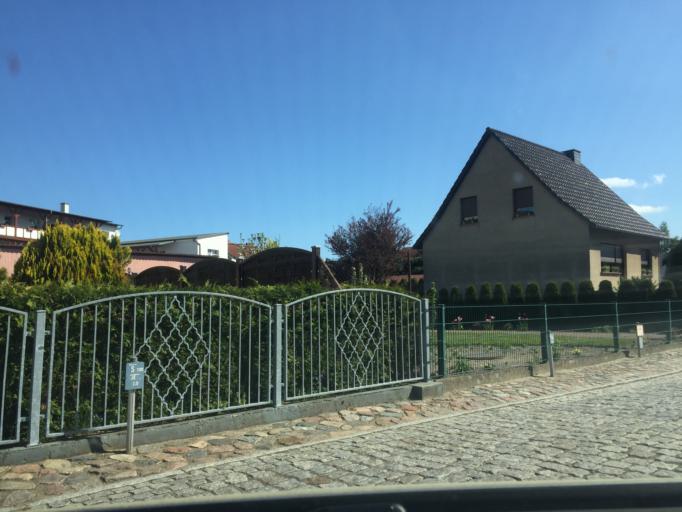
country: DE
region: Mecklenburg-Vorpommern
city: Torgelow
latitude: 53.6282
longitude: 14.0071
